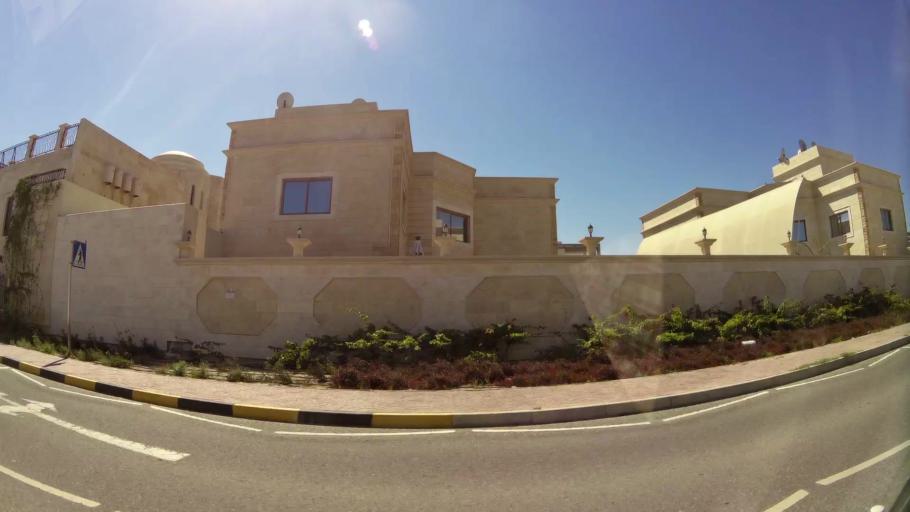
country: BH
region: Muharraq
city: Al Hadd
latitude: 26.2943
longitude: 50.6731
